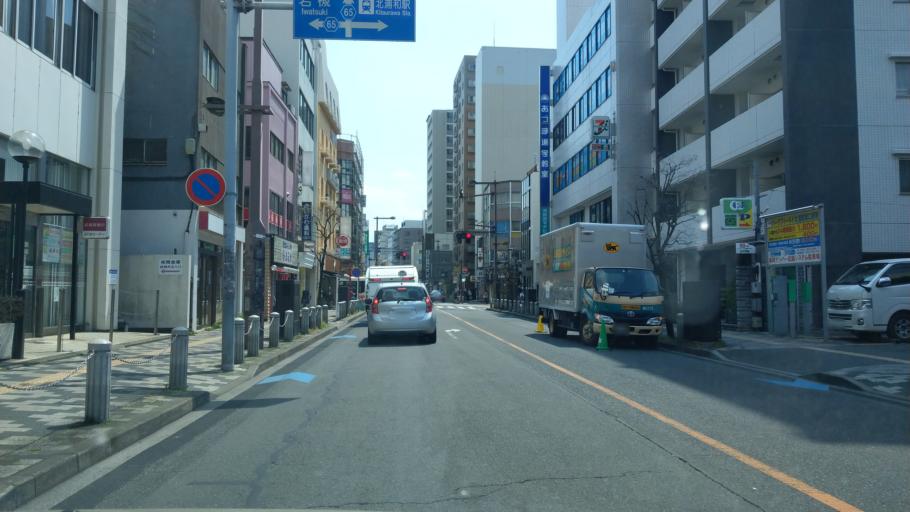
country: JP
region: Saitama
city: Yono
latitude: 35.8733
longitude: 139.6469
